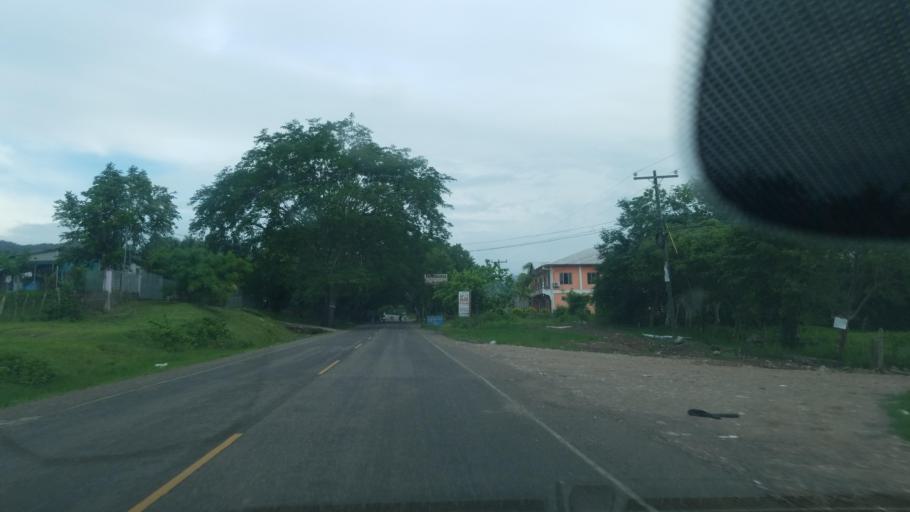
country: HN
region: Santa Barbara
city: San Vicente Centenario
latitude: 14.8834
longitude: -88.2487
